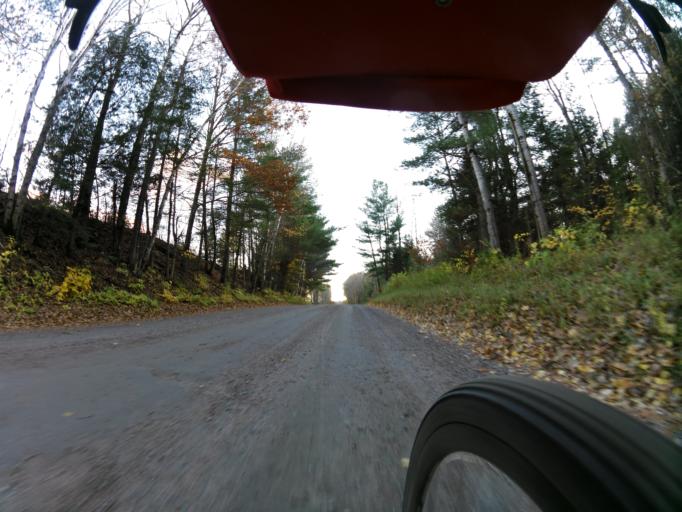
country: CA
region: Quebec
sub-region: Outaouais
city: Shawville
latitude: 45.6211
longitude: -76.3071
